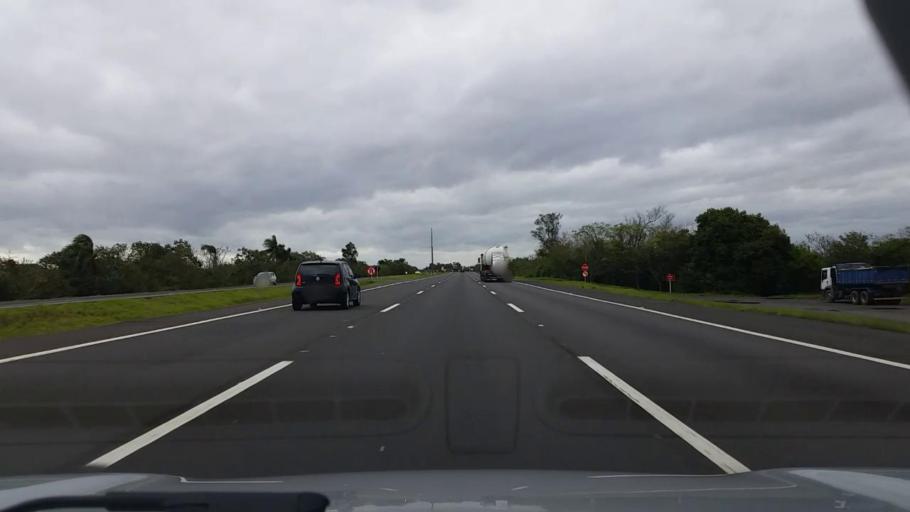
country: BR
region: Rio Grande do Sul
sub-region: Rolante
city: Rolante
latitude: -29.8837
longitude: -50.5588
